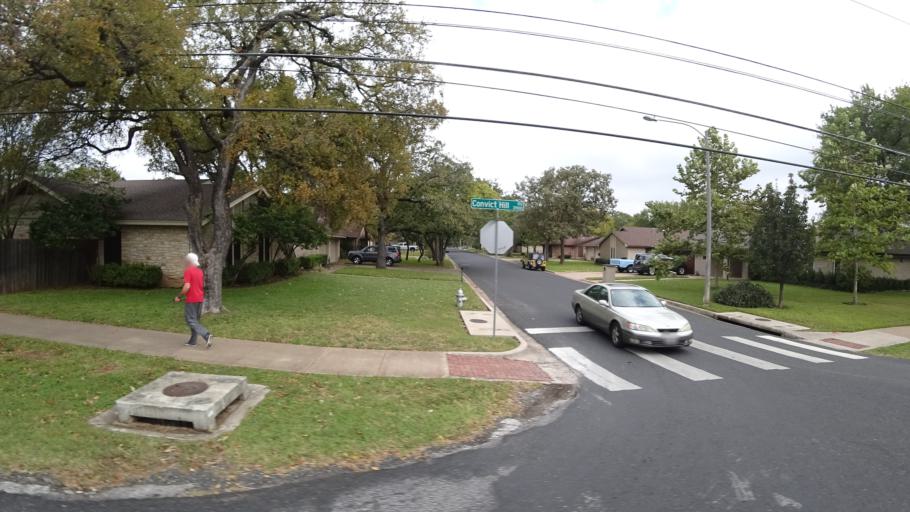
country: US
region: Texas
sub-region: Travis County
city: Shady Hollow
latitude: 30.2128
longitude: -97.8376
